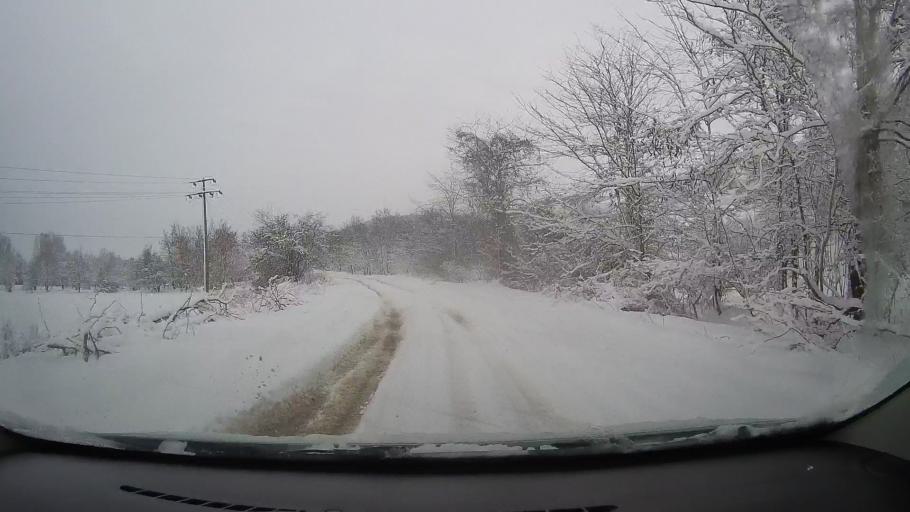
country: RO
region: Alba
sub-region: Comuna Pianu
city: Pianu de Jos
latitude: 45.9608
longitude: 23.4828
